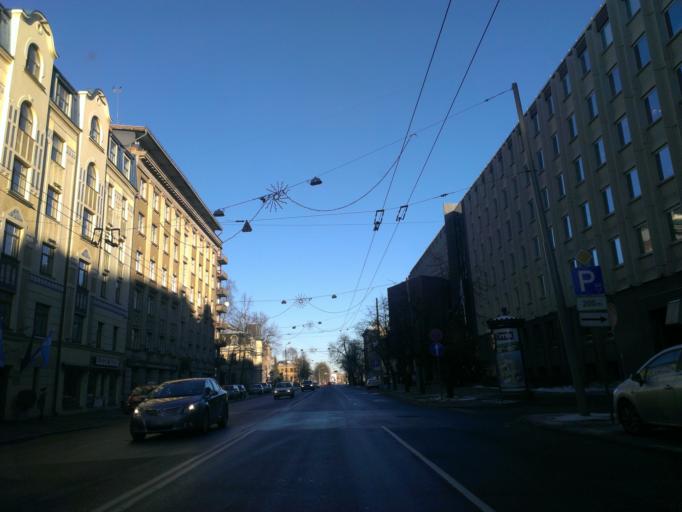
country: LV
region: Riga
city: Riga
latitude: 56.9601
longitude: 24.1057
